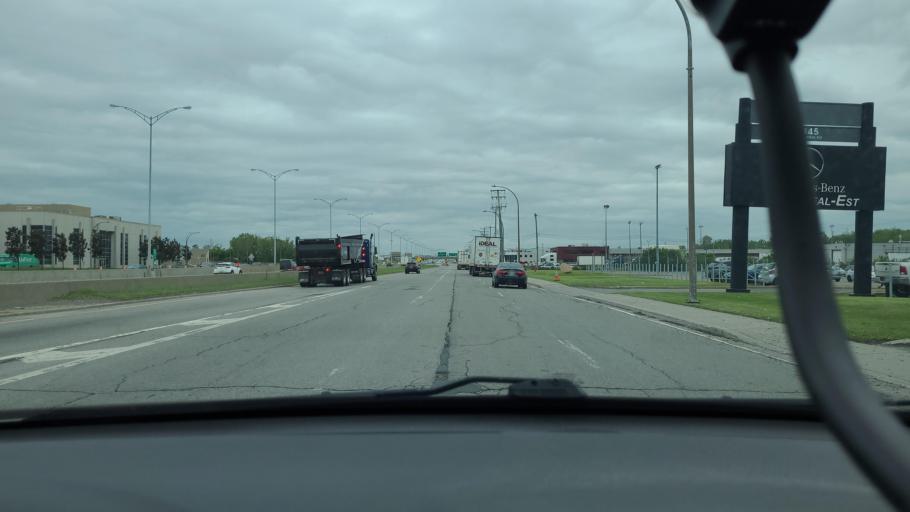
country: CA
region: Quebec
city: Montreal-Est
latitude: 45.6548
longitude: -73.5228
